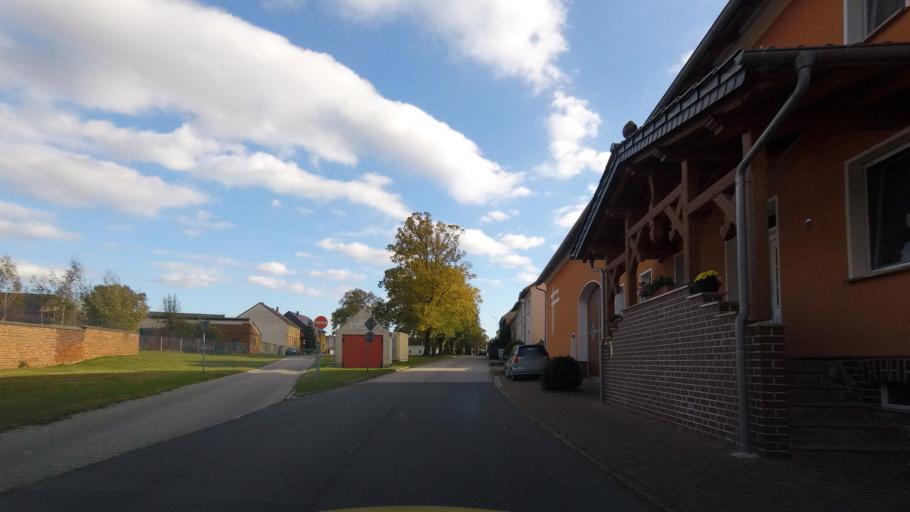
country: DE
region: Saxony-Anhalt
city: Seyda
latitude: 51.9490
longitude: 12.8665
